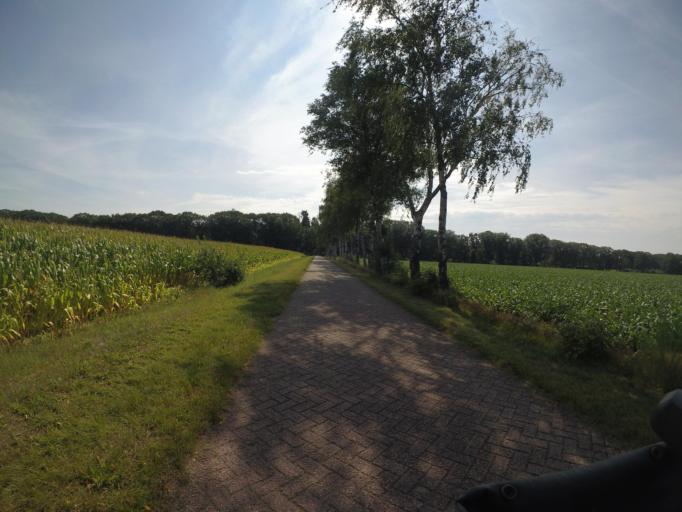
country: NL
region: North Brabant
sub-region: Bergeijk
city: Bergeyk
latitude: 51.3618
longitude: 5.3662
